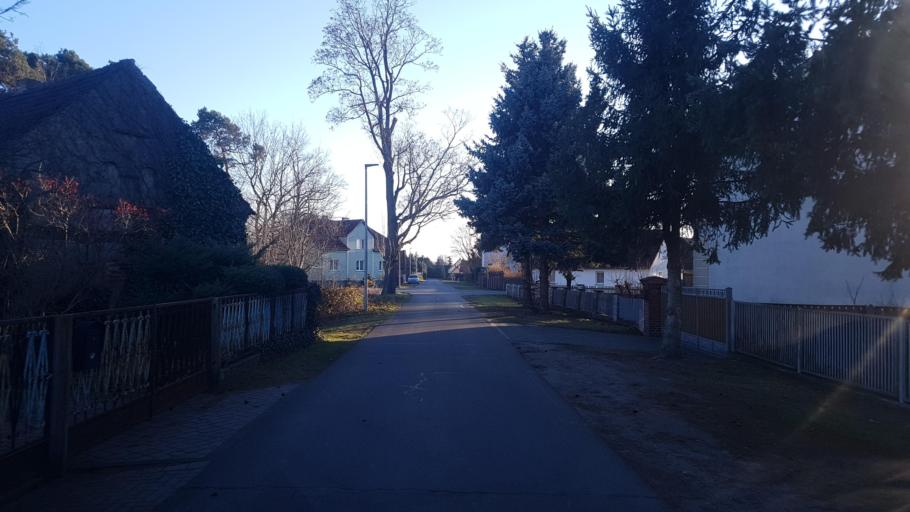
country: DE
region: Brandenburg
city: Peitz
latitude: 51.8861
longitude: 14.4183
